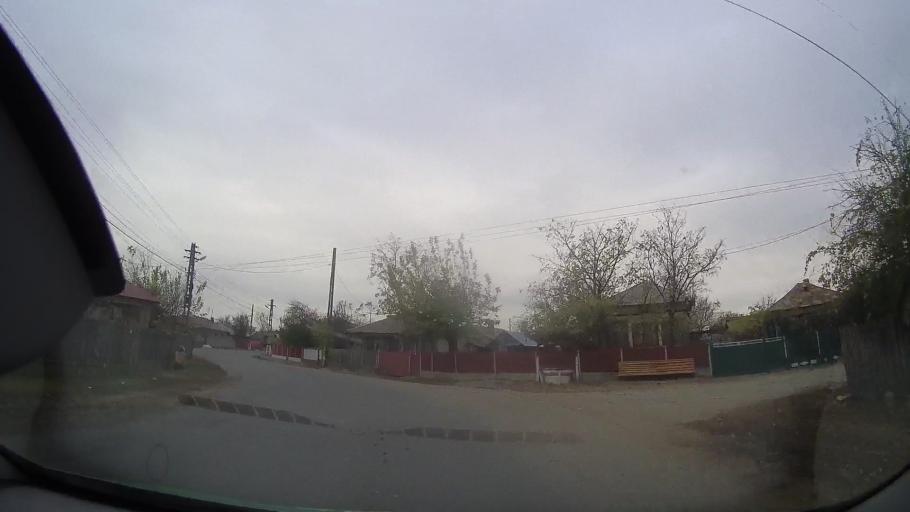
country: RO
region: Buzau
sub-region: Comuna Largu
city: Largu
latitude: 44.9757
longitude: 27.1437
